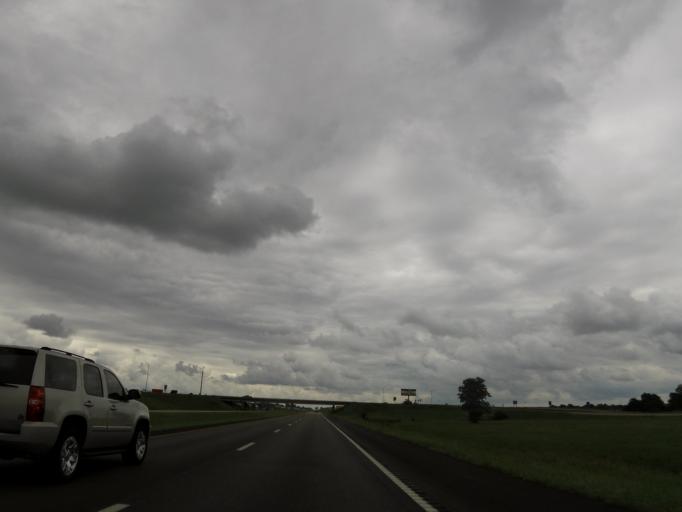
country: US
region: Missouri
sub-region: Mississippi County
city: Charleston
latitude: 36.9186
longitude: -89.3211
